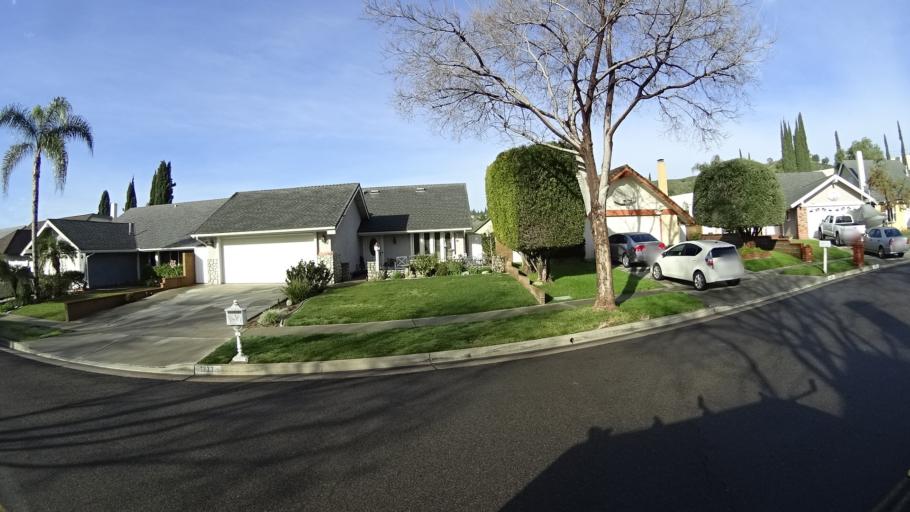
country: US
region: California
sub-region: Orange County
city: Yorba Linda
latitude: 33.8732
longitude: -117.7655
